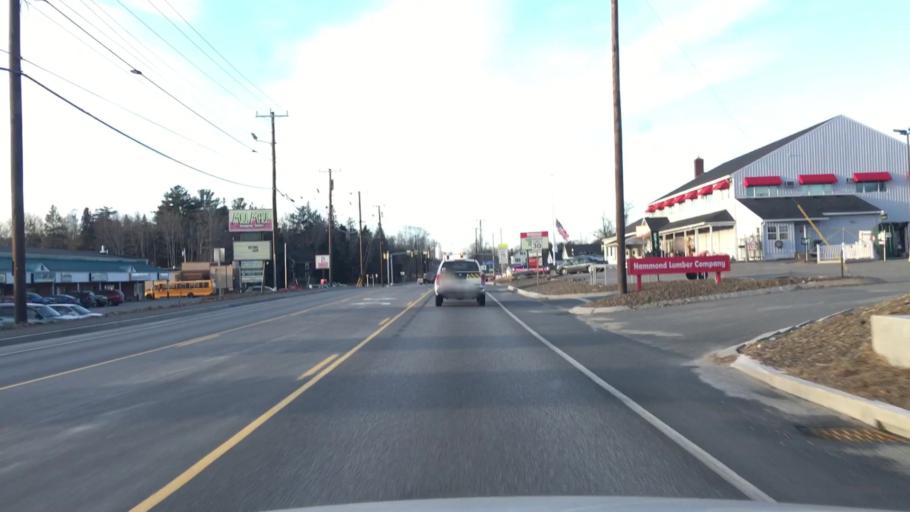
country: US
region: Maine
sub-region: Hancock County
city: Ellsworth
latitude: 44.5516
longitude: -68.4282
